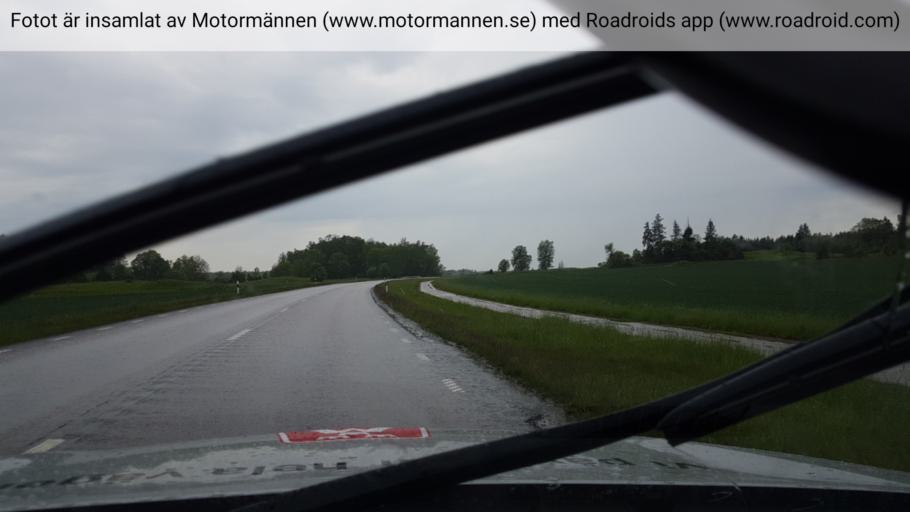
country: SE
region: Uppsala
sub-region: Uppsala Kommun
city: Uppsala
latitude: 59.8507
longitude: 17.4606
